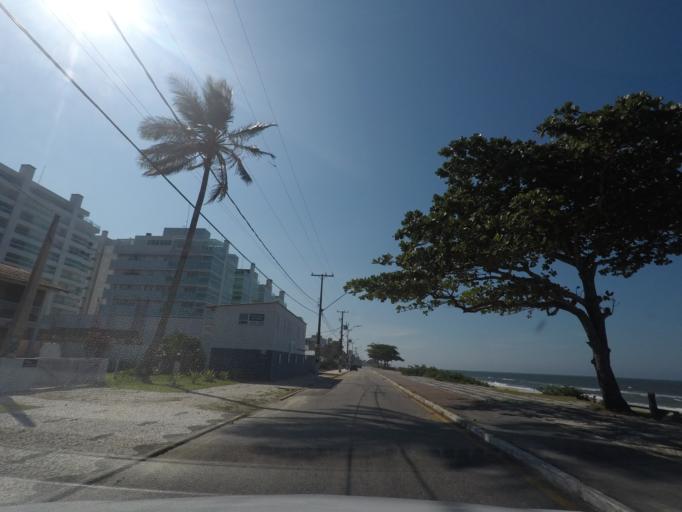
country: BR
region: Parana
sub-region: Guaratuba
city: Guaratuba
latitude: -25.8247
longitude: -48.5332
